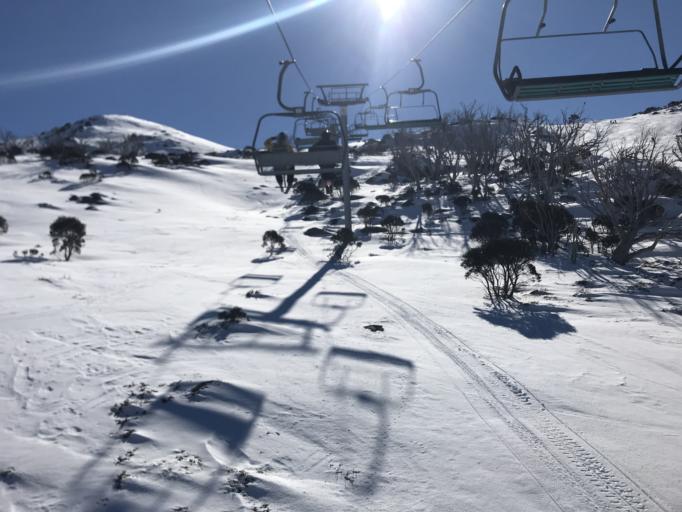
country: AU
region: New South Wales
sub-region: Snowy River
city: Jindabyne
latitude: -36.3816
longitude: 148.3974
